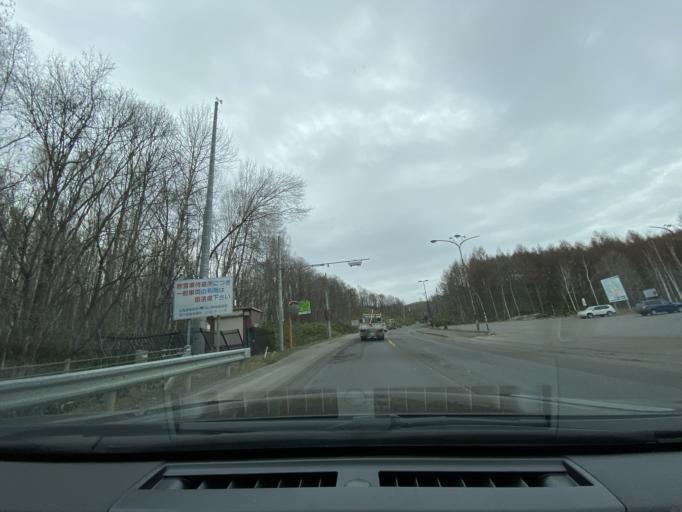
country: JP
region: Hokkaido
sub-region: Asahikawa-shi
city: Asahikawa
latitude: 43.9632
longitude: 142.4462
